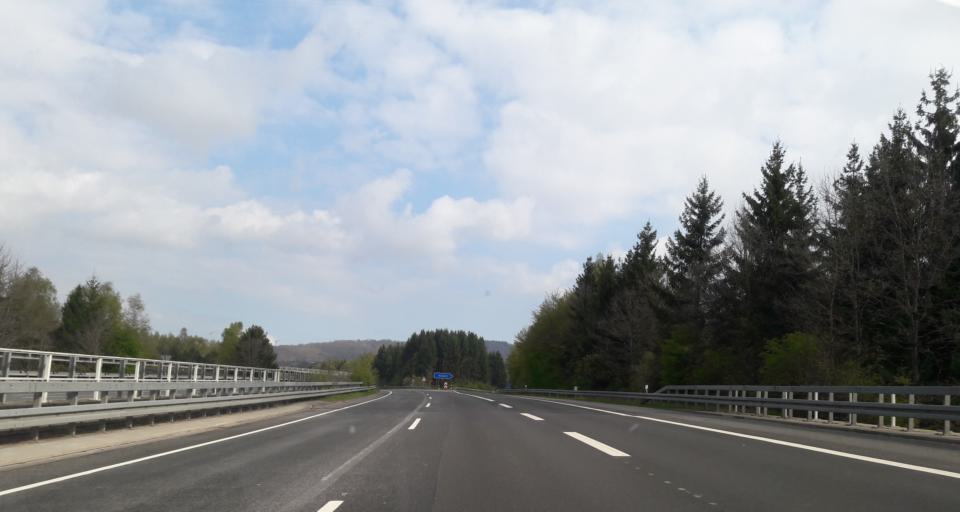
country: DE
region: Saarland
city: Nonnweiler
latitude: 49.5925
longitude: 6.9897
